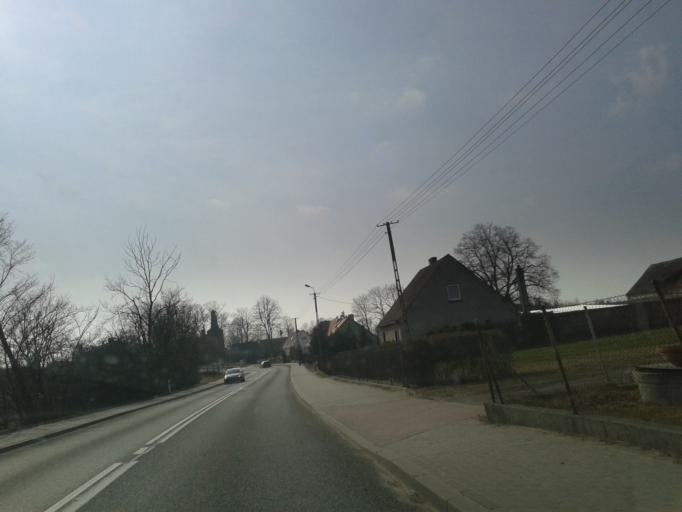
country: PL
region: Pomeranian Voivodeship
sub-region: Powiat czluchowski
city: Debrzno
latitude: 53.5997
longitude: 17.1357
